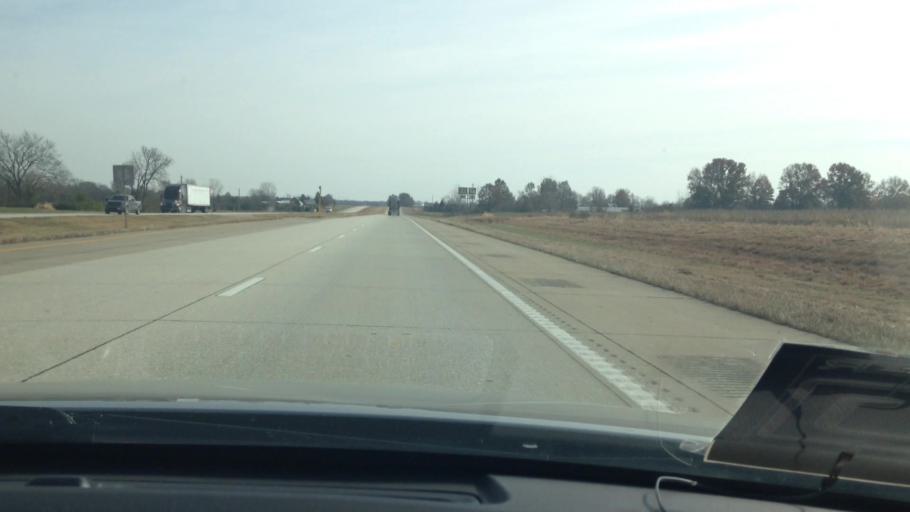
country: US
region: Missouri
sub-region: Henry County
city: Clinton
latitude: 38.4346
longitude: -93.9349
